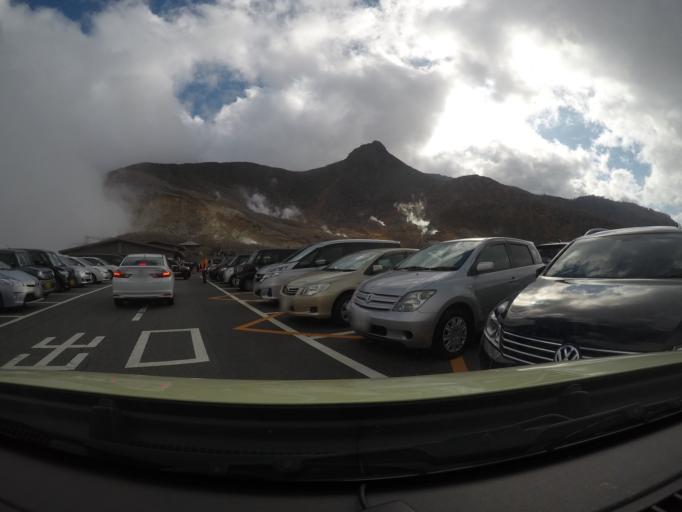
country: JP
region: Kanagawa
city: Hakone
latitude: 35.2432
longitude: 139.0192
